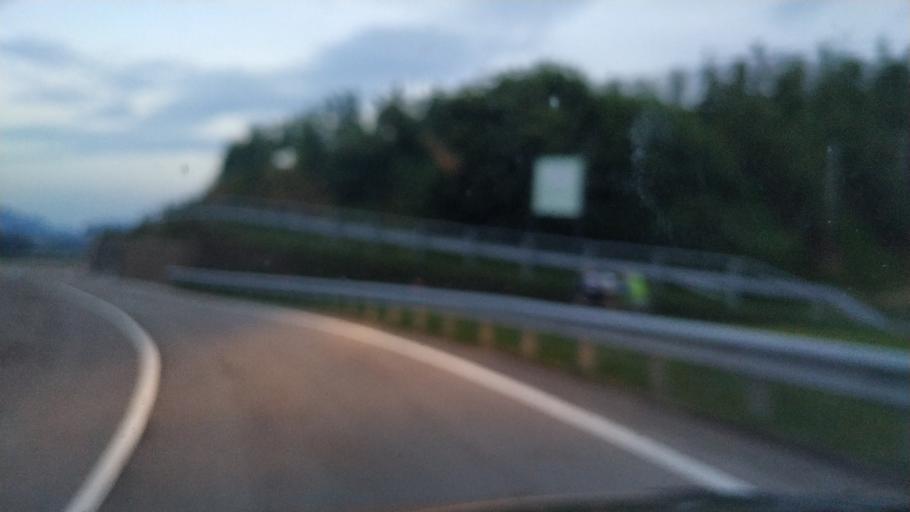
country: IT
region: Trentino-Alto Adige
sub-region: Provincia di Trento
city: Cloz
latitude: 46.4134
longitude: 11.0809
